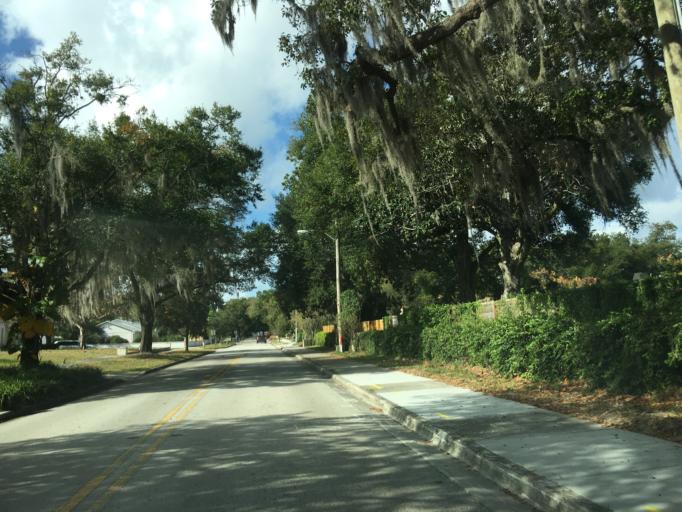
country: US
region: Florida
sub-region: Orange County
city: Maitland
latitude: 28.6102
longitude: -81.3598
